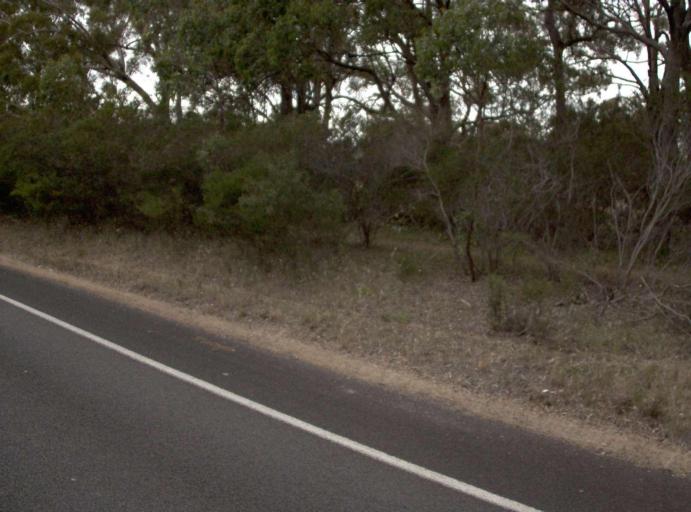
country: AU
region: Victoria
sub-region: Wellington
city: Sale
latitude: -38.4477
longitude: 146.9423
